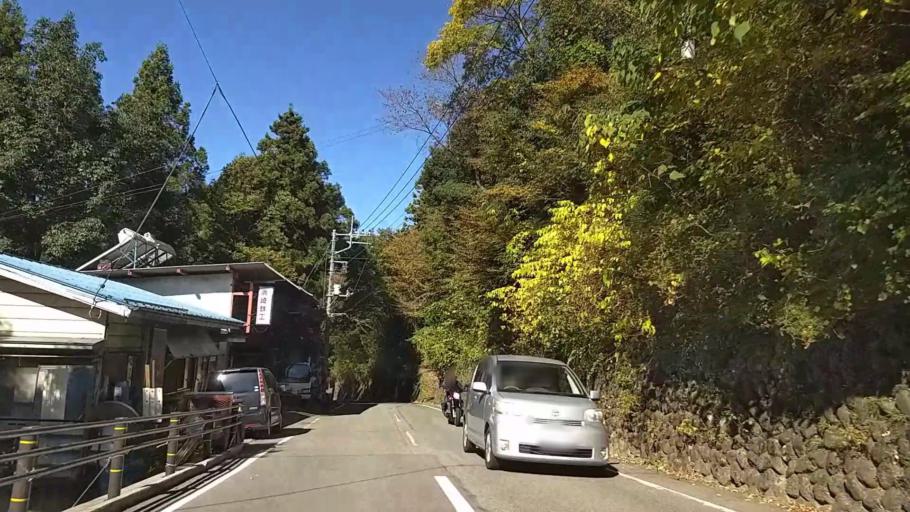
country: JP
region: Yamanashi
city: Uenohara
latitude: 35.6417
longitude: 139.1024
